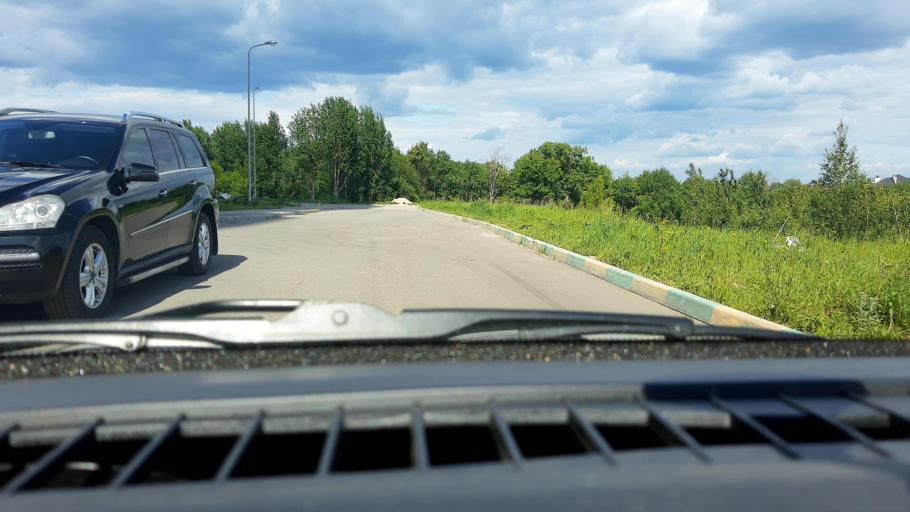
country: RU
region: Nizjnij Novgorod
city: Afonino
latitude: 56.2990
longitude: 44.0863
